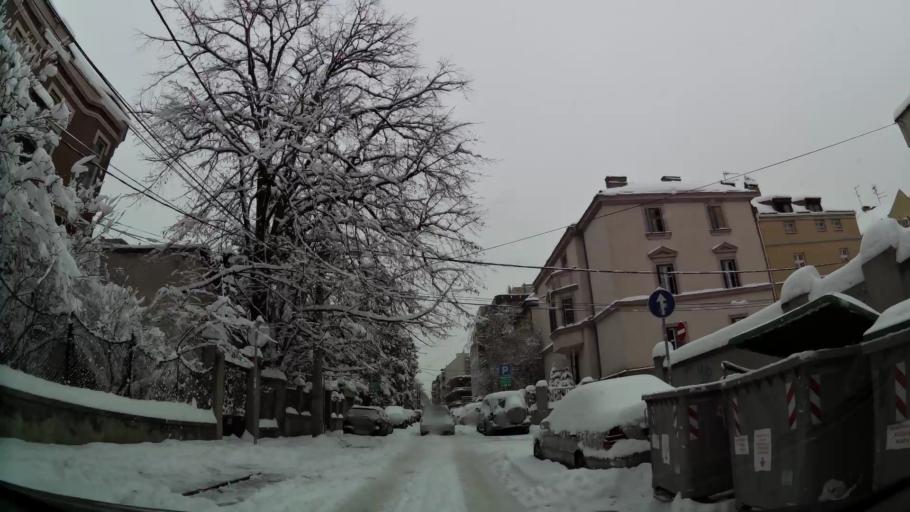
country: RS
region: Central Serbia
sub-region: Belgrade
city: Vracar
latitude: 44.7962
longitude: 20.4680
